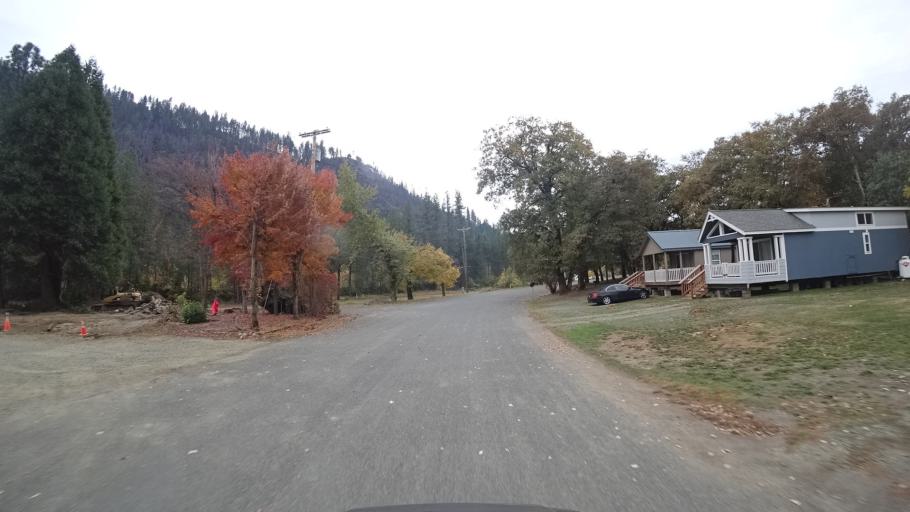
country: US
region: California
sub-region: Siskiyou County
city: Happy Camp
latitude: 41.7908
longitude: -123.3813
